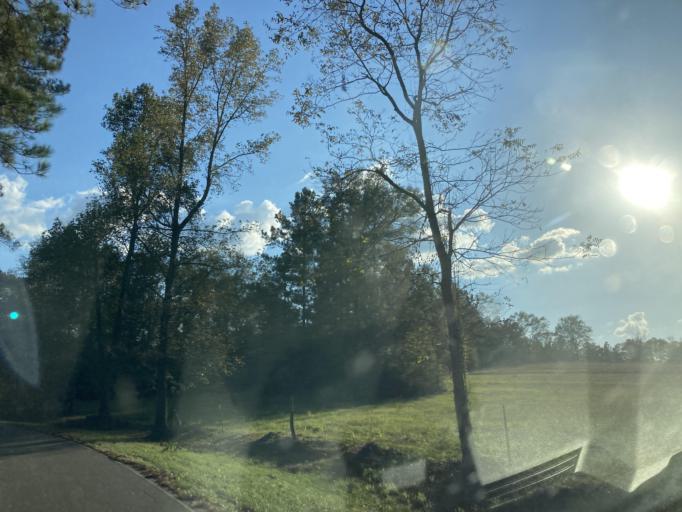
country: US
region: Mississippi
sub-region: Lamar County
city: Sumrall
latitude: 31.4000
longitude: -89.6503
